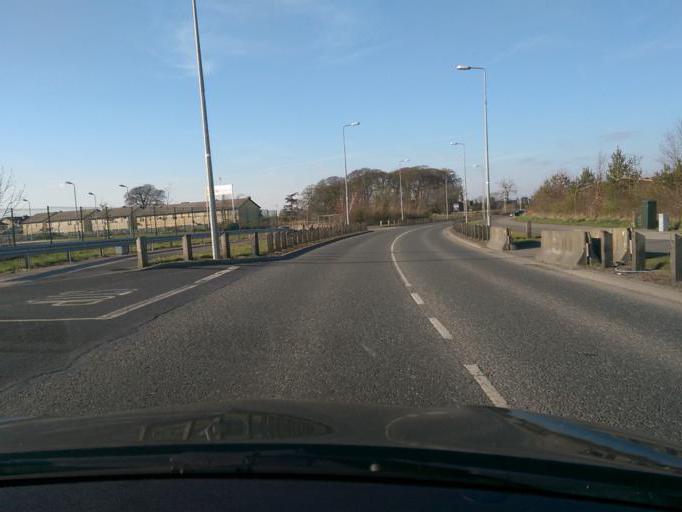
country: IE
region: Leinster
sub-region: Kildare
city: Naas
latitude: 53.2109
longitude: -6.6804
